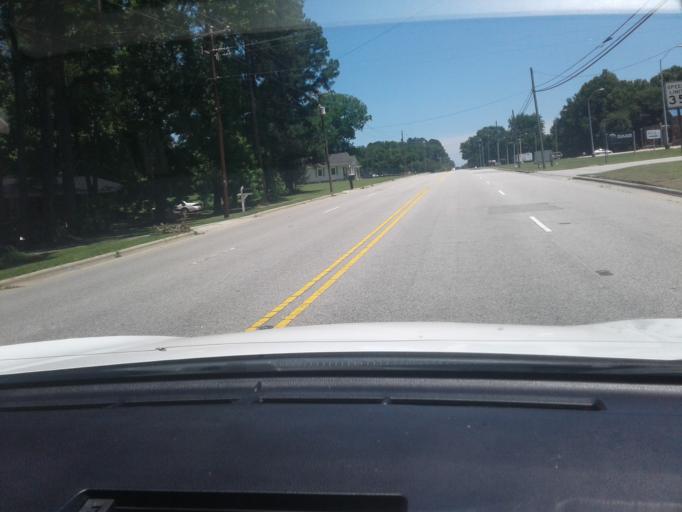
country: US
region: North Carolina
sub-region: Harnett County
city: Lillington
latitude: 35.3917
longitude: -78.8104
